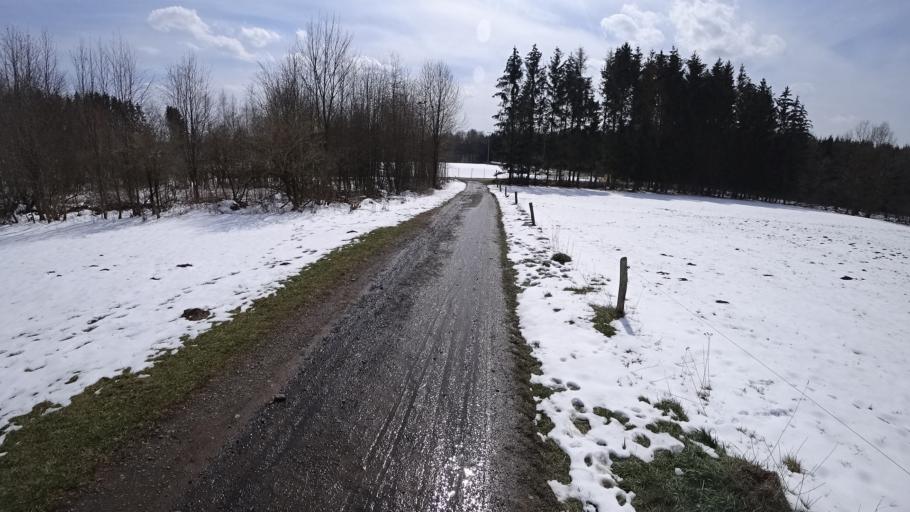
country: DE
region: Rheinland-Pfalz
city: Morlen
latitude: 50.7061
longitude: 7.8824
